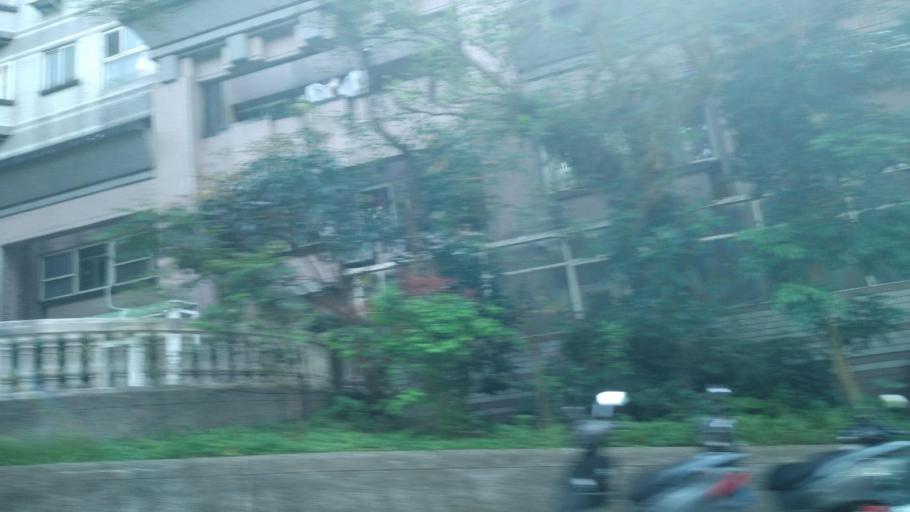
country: TW
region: Taipei
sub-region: Taipei
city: Banqiao
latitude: 24.9406
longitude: 121.5025
